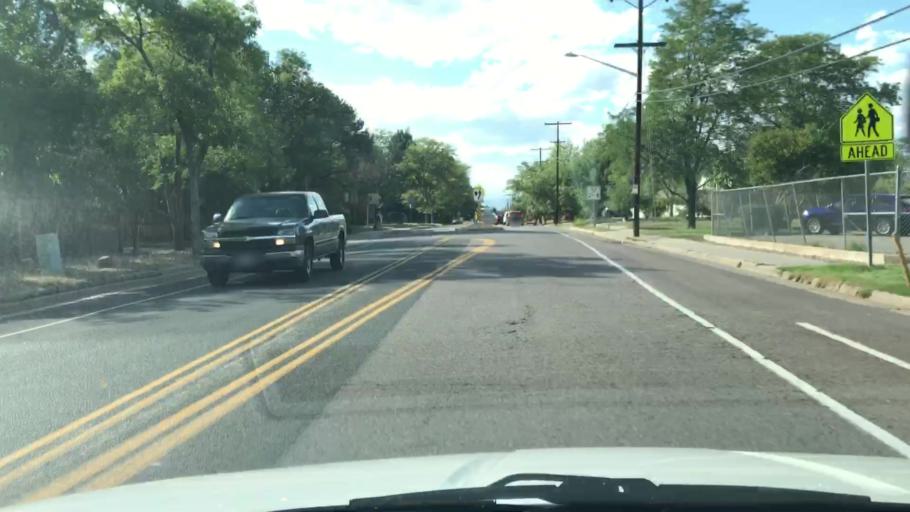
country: US
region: Colorado
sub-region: Arapahoe County
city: Cherry Hills Village
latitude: 39.6456
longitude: -104.9221
